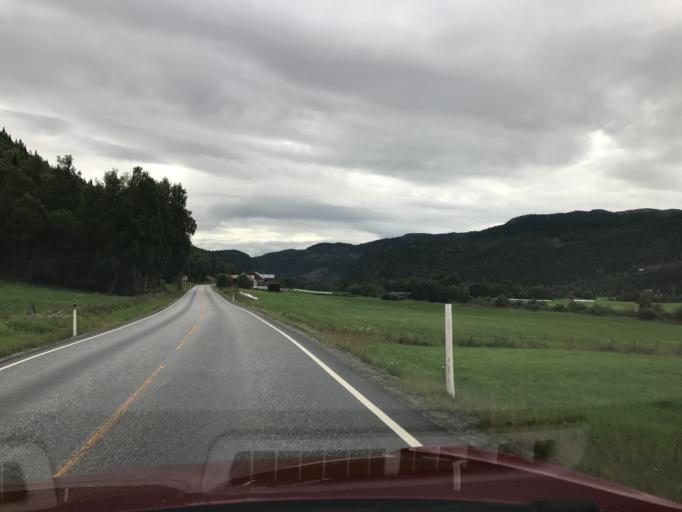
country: NO
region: Buskerud
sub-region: Nore og Uvdal
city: Rodberg
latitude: 60.2610
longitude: 8.8526
